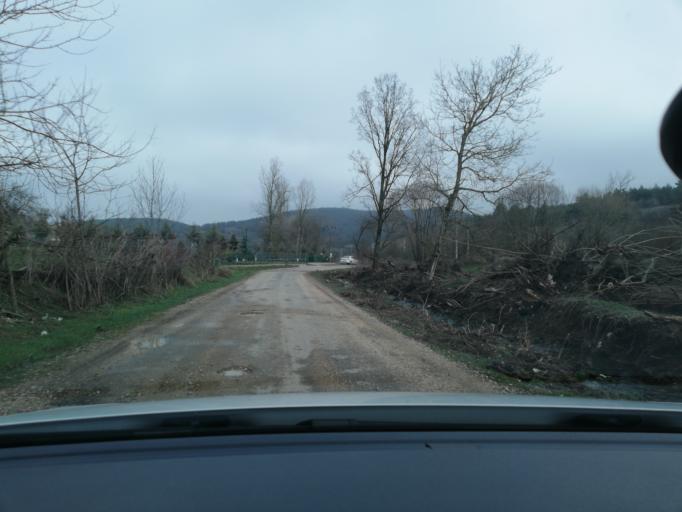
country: TR
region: Bolu
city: Bolu
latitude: 40.6756
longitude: 31.4724
